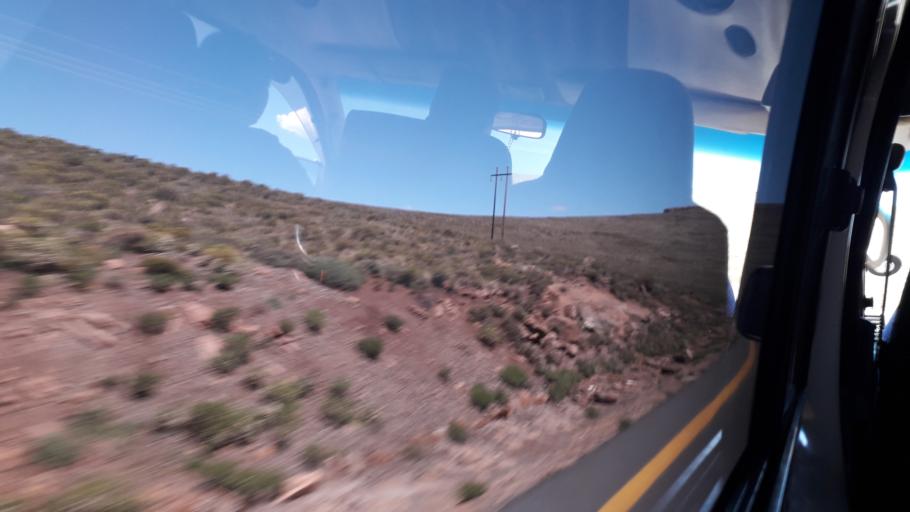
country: LS
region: Mokhotlong
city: Mokhotlong
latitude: -29.0643
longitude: 28.8507
